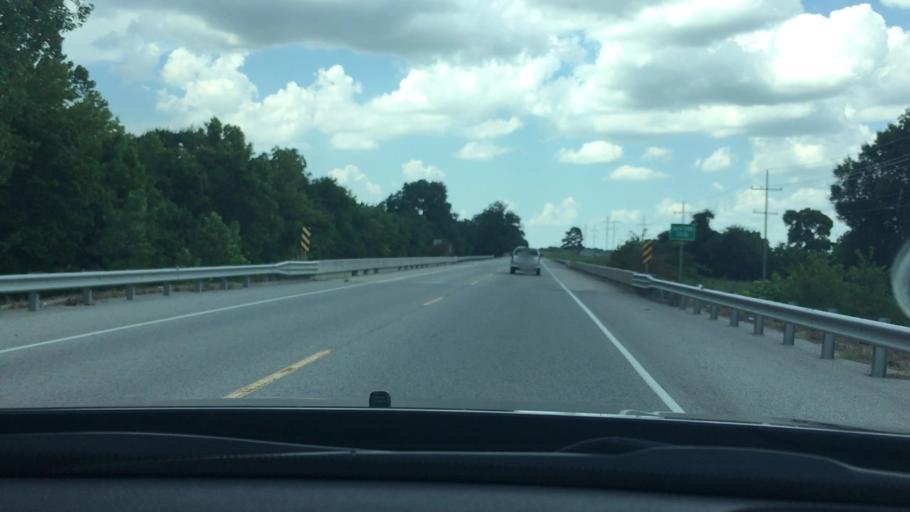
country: US
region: Oklahoma
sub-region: Pontotoc County
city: Ada
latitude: 34.6851
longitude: -96.6348
